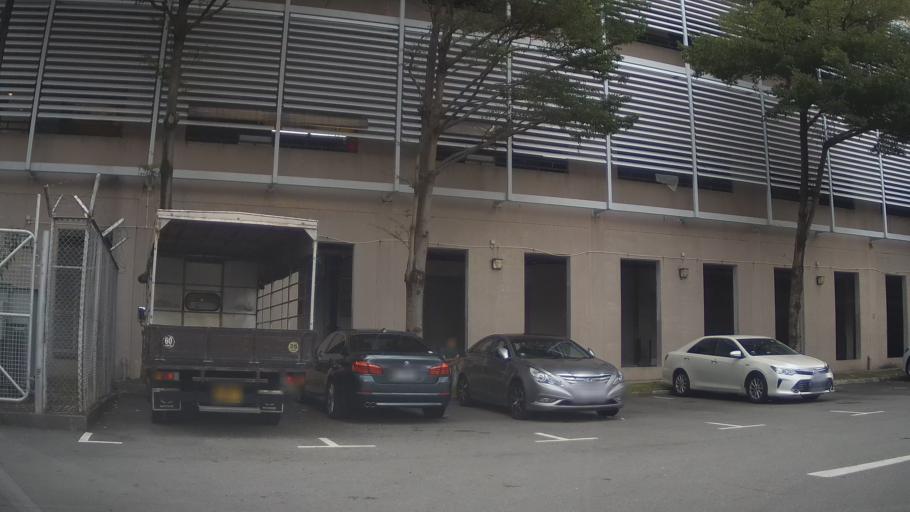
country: SG
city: Singapore
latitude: 1.3344
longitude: 103.7218
